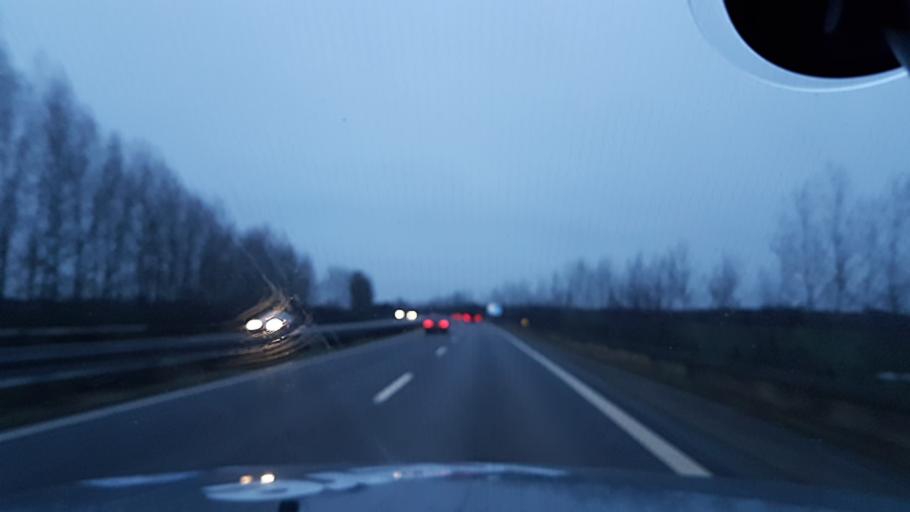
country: DK
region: Zealand
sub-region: Faxe Kommune
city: Ronnede
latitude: 55.2176
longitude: 11.9754
